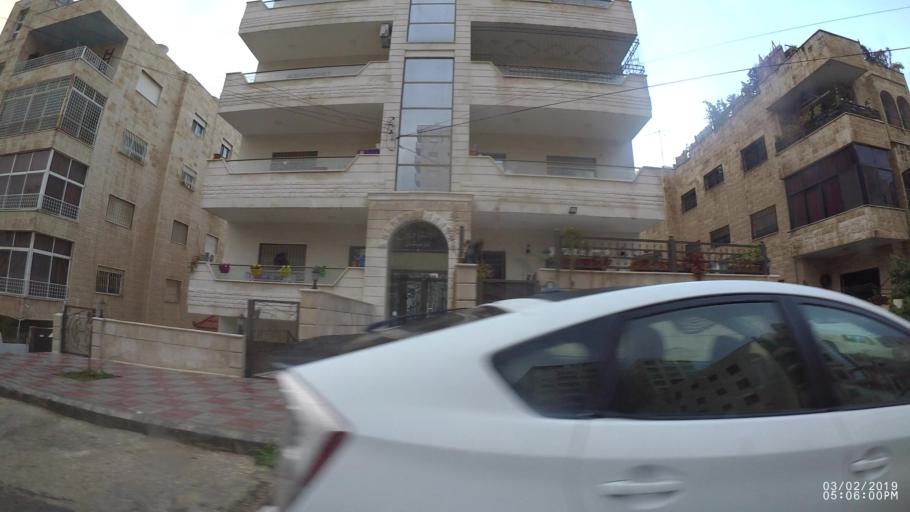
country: JO
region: Amman
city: Amman
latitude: 31.9874
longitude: 35.9157
